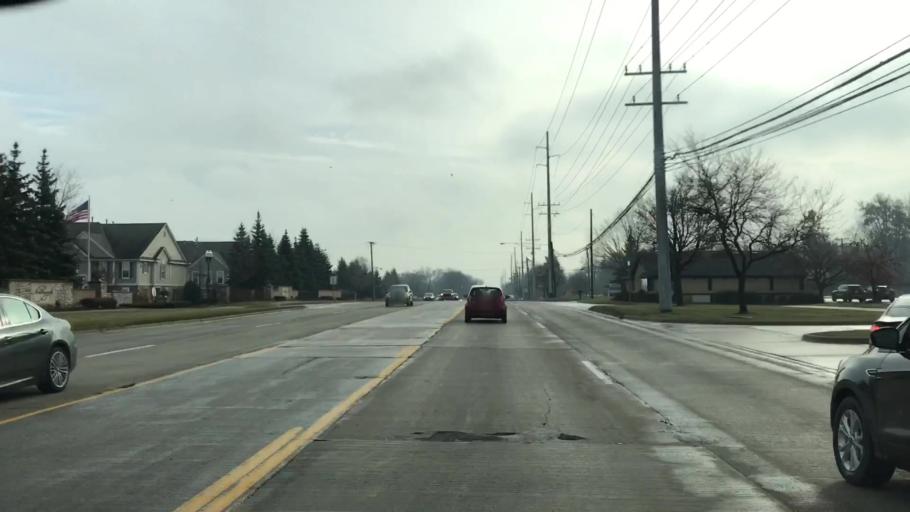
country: US
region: Michigan
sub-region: Oakland County
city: Troy
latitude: 42.6186
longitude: -83.1304
